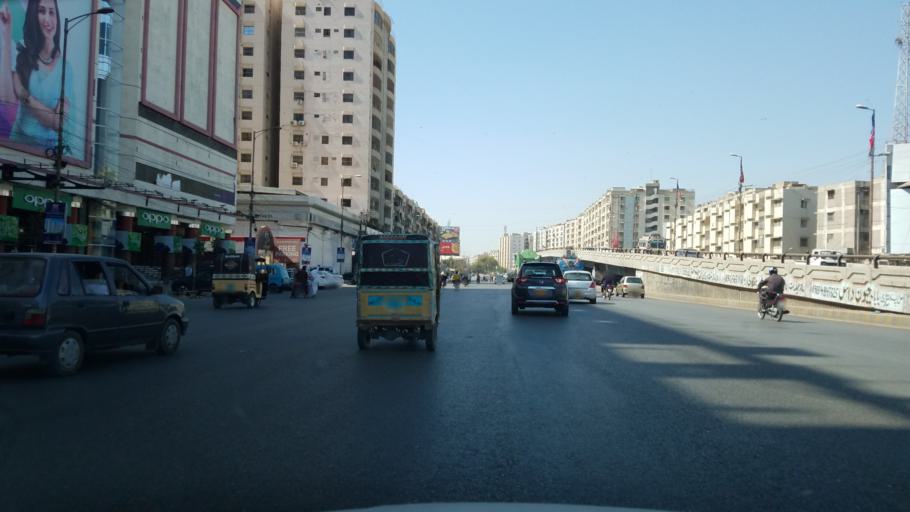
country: PK
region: Sindh
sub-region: Karachi District
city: Karachi
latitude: 24.9029
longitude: 67.1147
